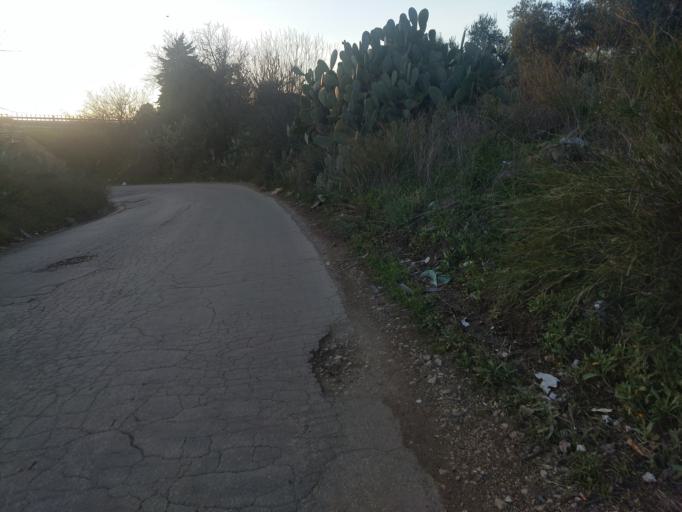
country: IT
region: Apulia
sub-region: Provincia di Bari
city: Modugno
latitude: 41.0873
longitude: 16.8046
